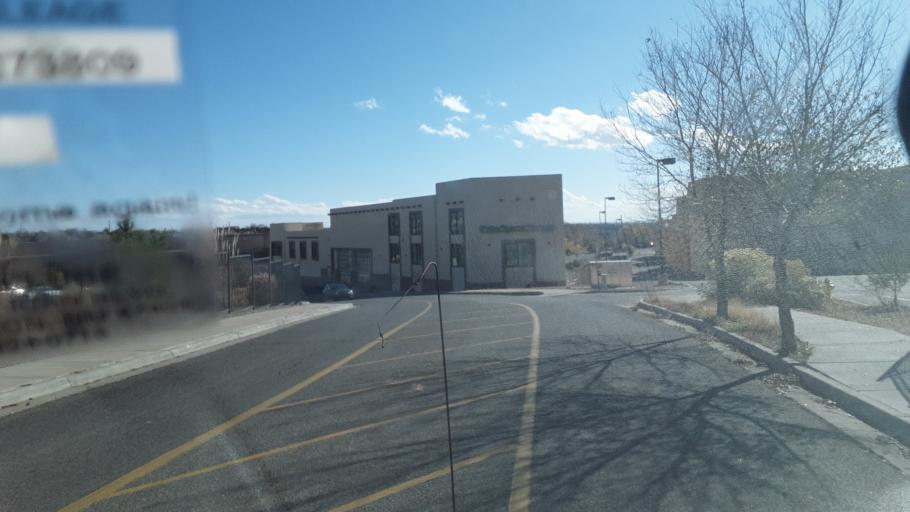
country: US
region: New Mexico
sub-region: Santa Fe County
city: Agua Fria
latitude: 35.6427
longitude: -106.0094
